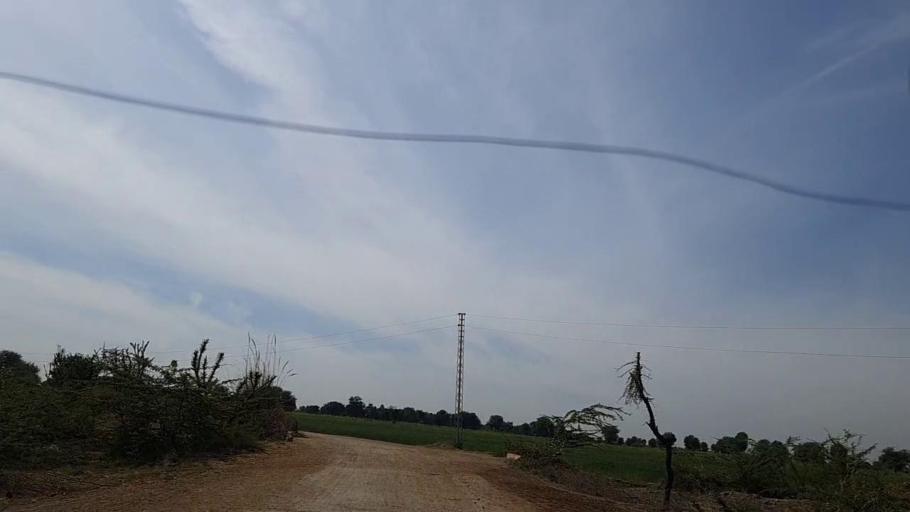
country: PK
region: Sindh
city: Dhoro Naro
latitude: 25.4924
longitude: 69.4921
